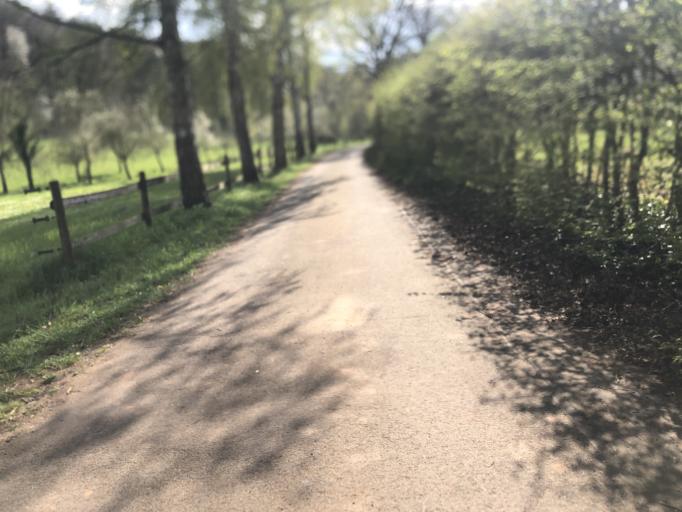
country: DE
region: North Rhine-Westphalia
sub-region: Regierungsbezirk Koln
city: Mechernich
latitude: 50.6213
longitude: 6.6182
